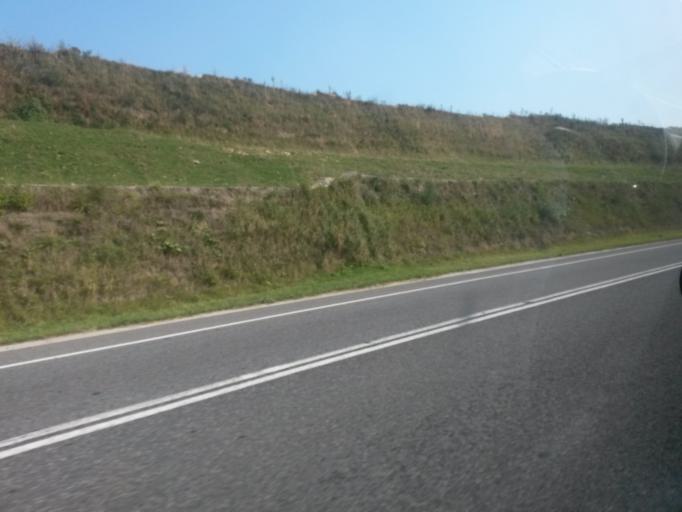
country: RO
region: Cluj
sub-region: Comuna Feleacu
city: Gheorghieni
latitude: 46.7138
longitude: 23.6625
